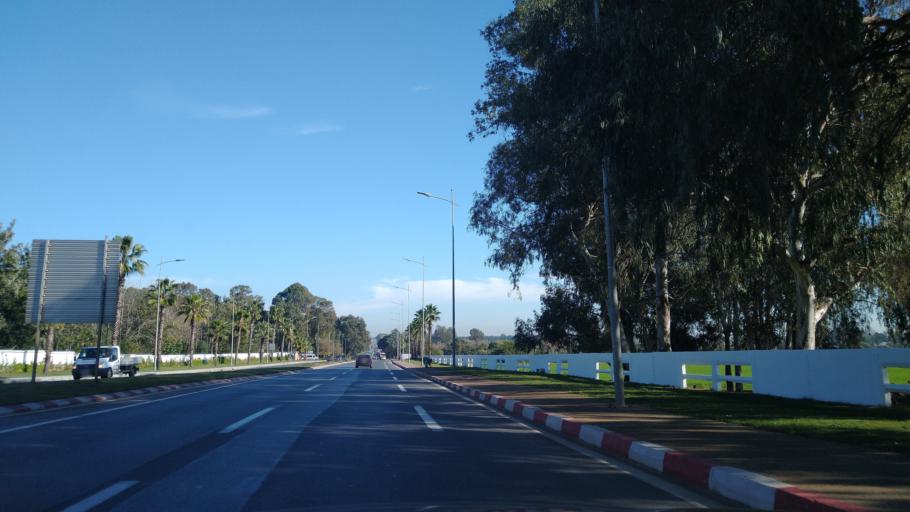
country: MA
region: Rabat-Sale-Zemmour-Zaer
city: Sale
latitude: 34.0307
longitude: -6.7528
